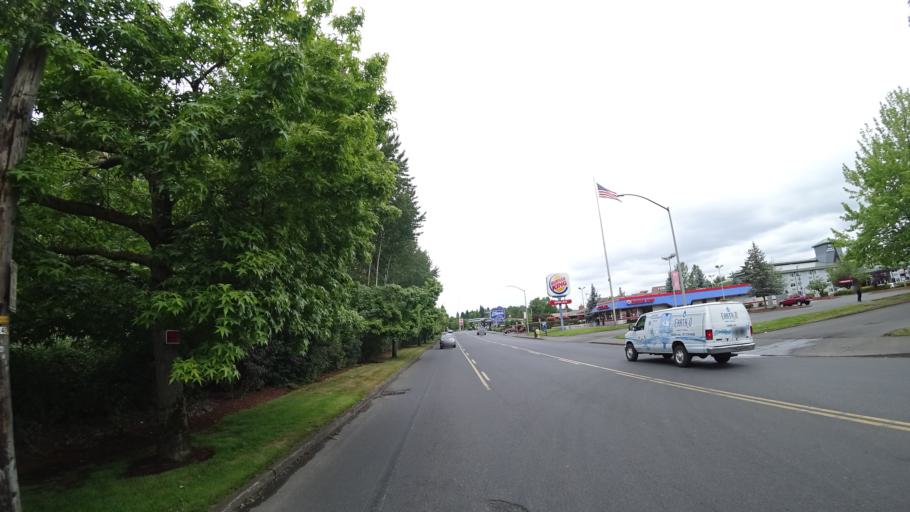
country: US
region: Washington
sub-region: Clark County
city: Vancouver
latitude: 45.5932
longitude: -122.6818
